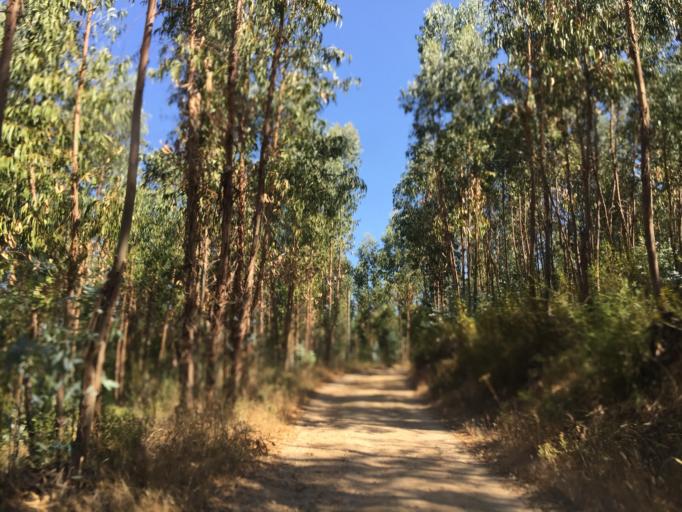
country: PT
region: Santarem
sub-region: Tomar
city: Tomar
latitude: 39.6090
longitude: -8.3491
